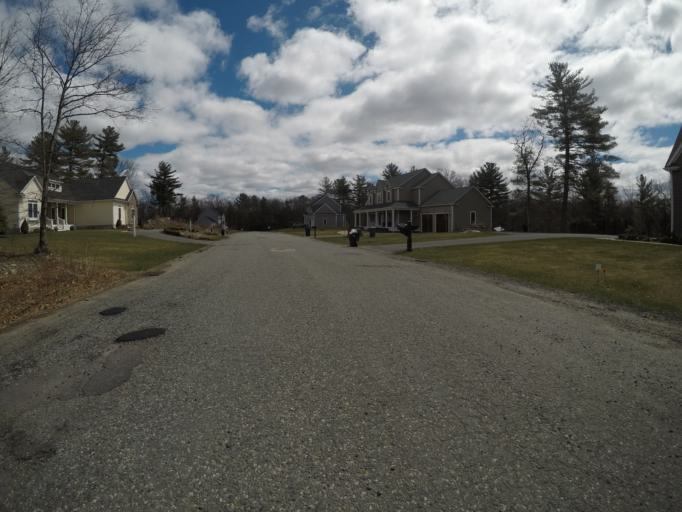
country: US
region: Massachusetts
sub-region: Norfolk County
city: Stoughton
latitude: 42.0786
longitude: -71.0754
